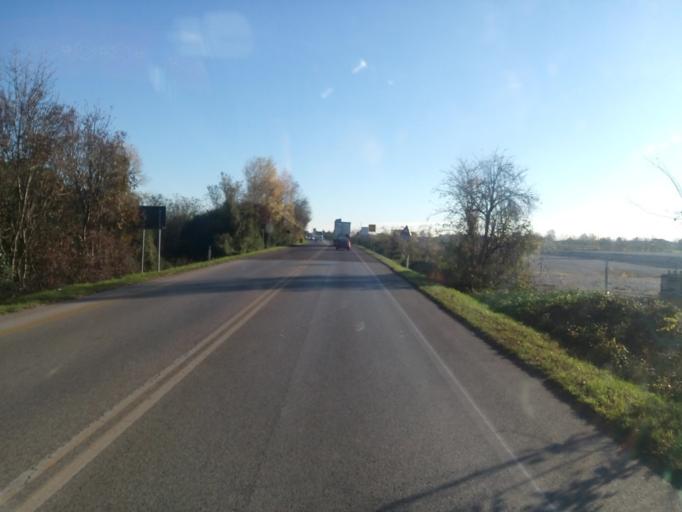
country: IT
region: Veneto
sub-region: Provincia di Vicenza
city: Cartigliano
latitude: 45.7378
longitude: 11.7094
